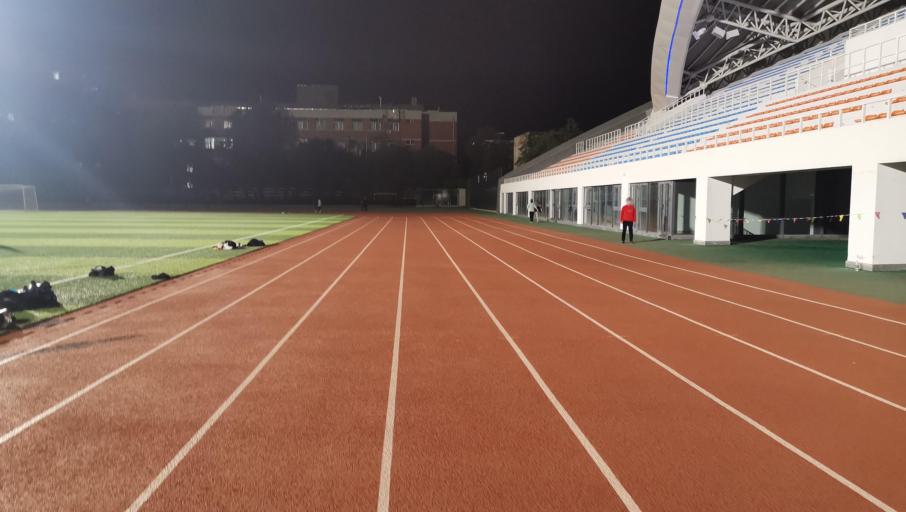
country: CN
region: Shandong Sheng
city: Jinan
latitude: 36.6507
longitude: 117.0123
